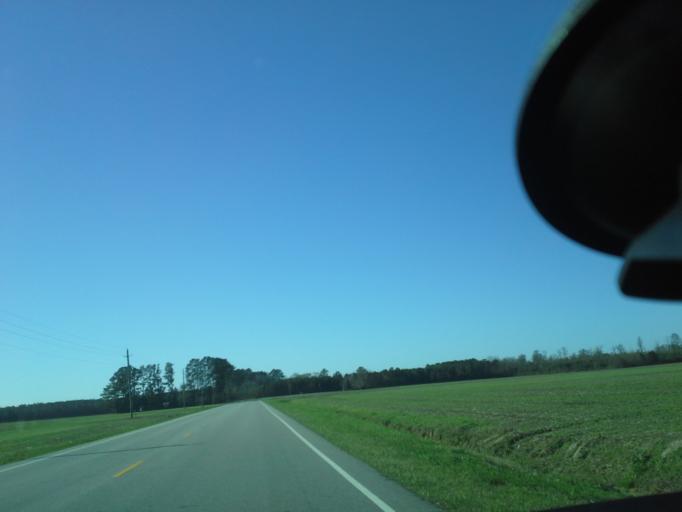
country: US
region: North Carolina
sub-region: Beaufort County
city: Belhaven
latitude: 35.5276
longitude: -76.7622
